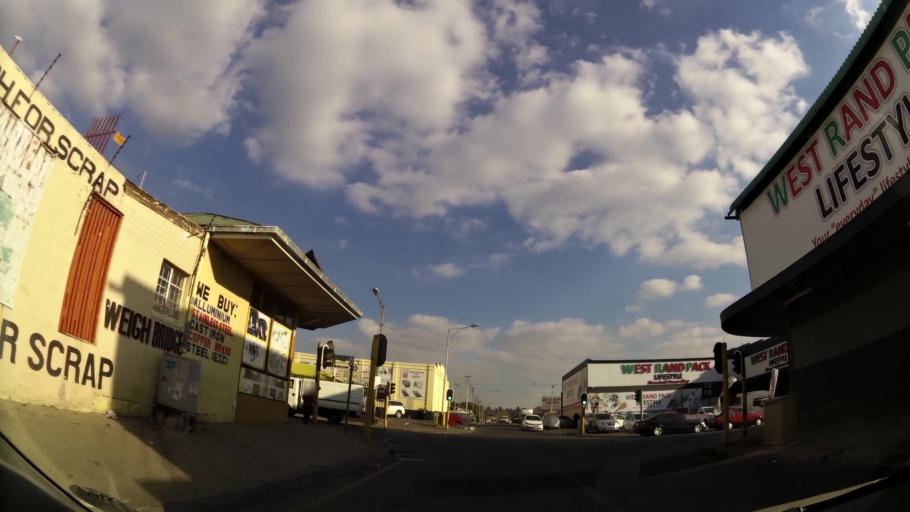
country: ZA
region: Gauteng
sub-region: West Rand District Municipality
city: Krugersdorp
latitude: -26.0980
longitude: 27.7601
